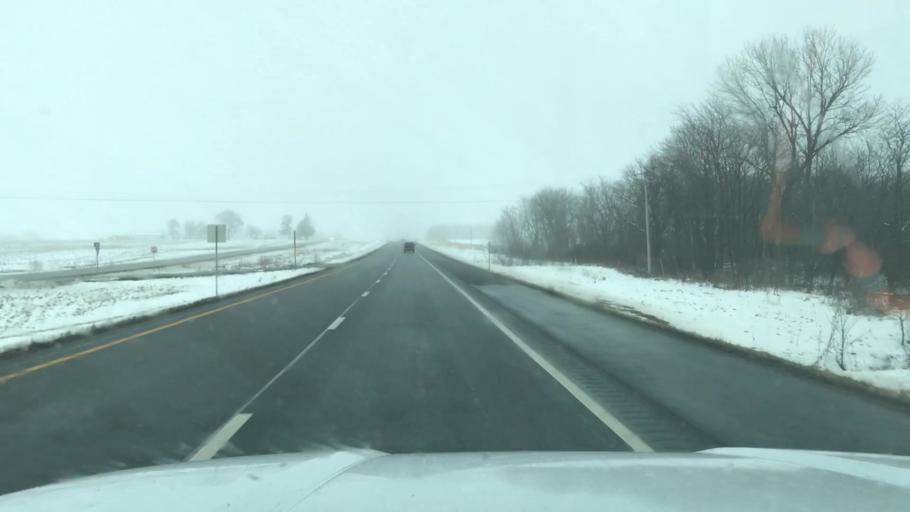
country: US
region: Missouri
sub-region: DeKalb County
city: Maysville
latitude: 39.7614
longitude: -94.3946
